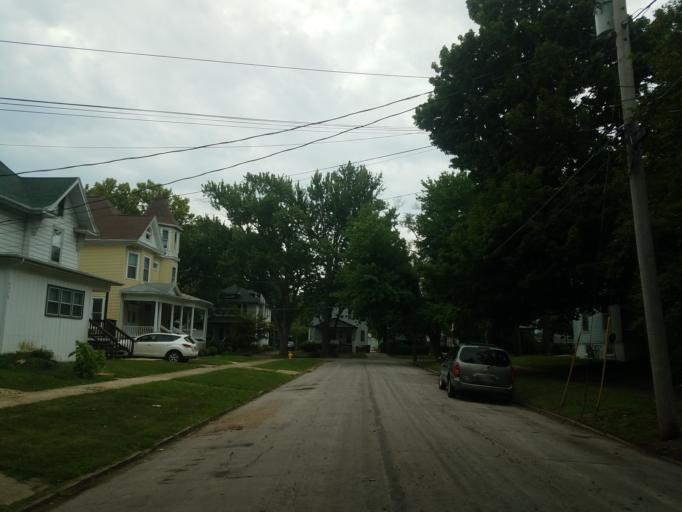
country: US
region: Illinois
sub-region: McLean County
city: Bloomington
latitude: 40.4864
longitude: -88.9832
